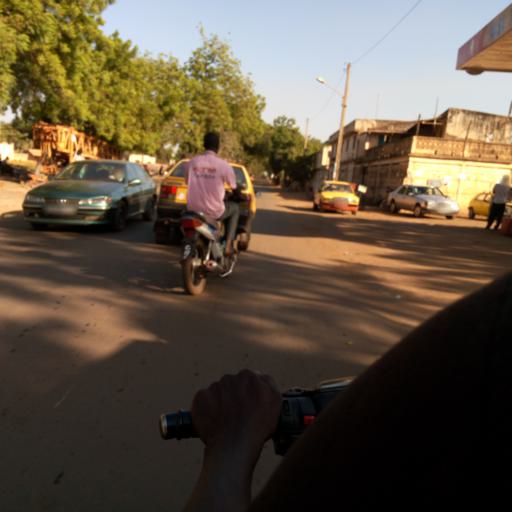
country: ML
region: Bamako
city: Bamako
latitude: 12.6572
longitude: -8.0290
